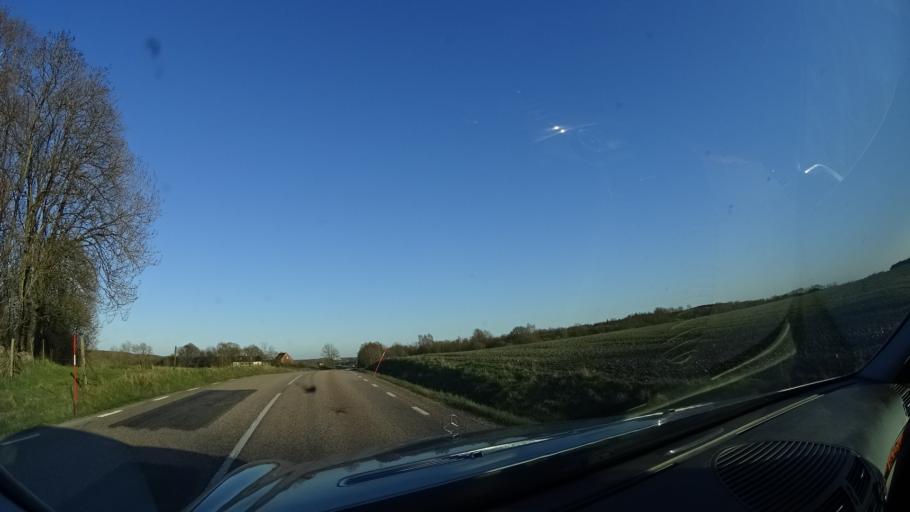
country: SE
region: Skane
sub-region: Bjuvs Kommun
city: Billesholm
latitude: 56.0279
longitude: 13.0412
